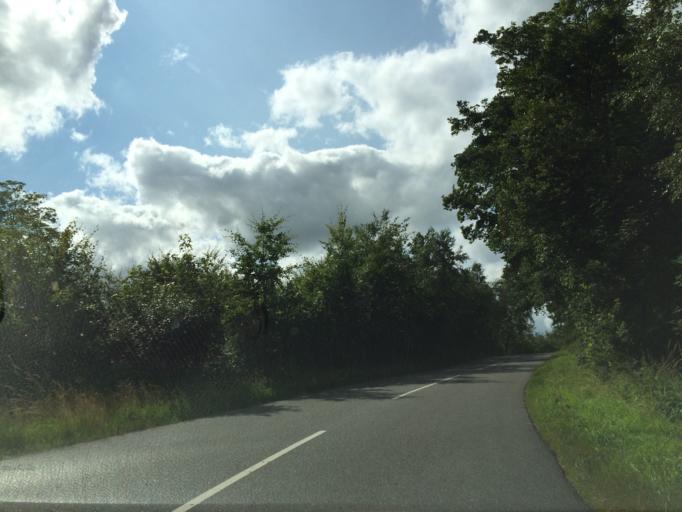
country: DK
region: Central Jutland
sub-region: Silkeborg Kommune
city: Svejbaek
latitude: 56.2291
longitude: 9.7266
